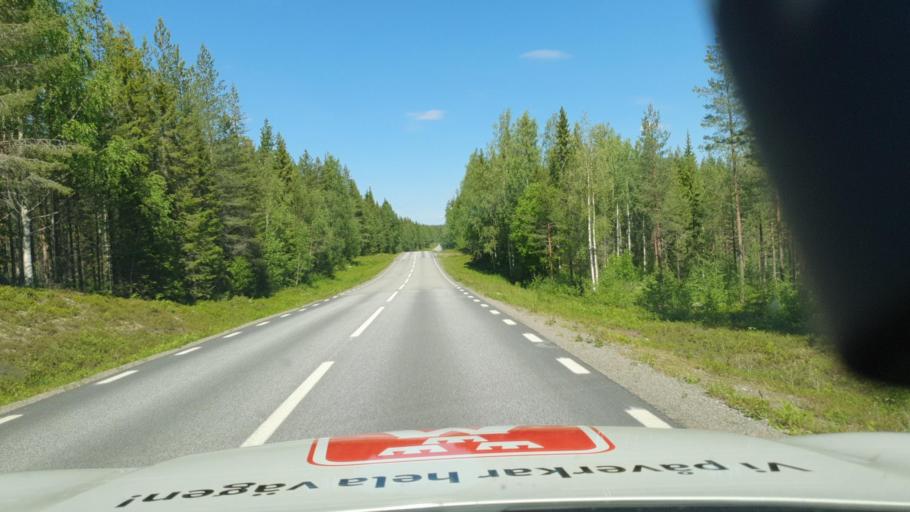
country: SE
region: Vaesterbotten
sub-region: Skelleftea Kommun
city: Boliden
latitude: 64.8310
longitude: 20.3713
